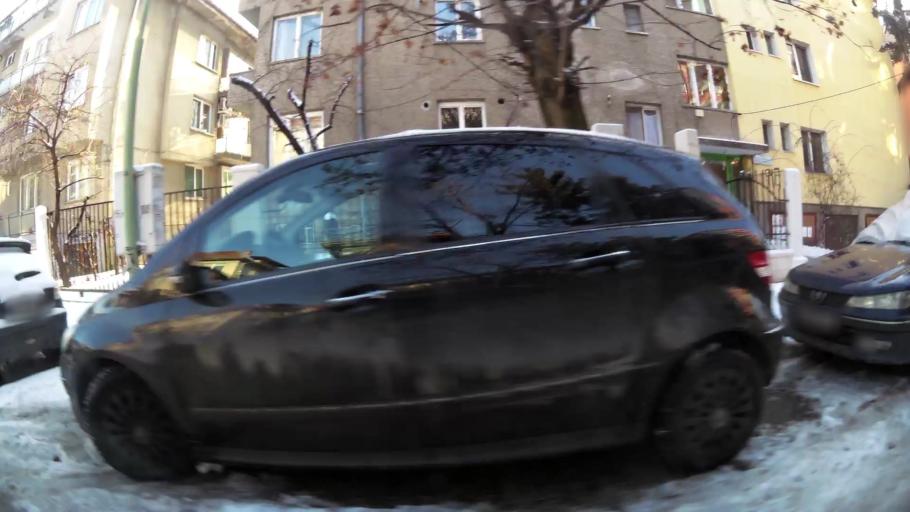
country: BG
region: Sofia-Capital
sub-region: Stolichna Obshtina
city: Sofia
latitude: 42.6769
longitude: 23.3618
